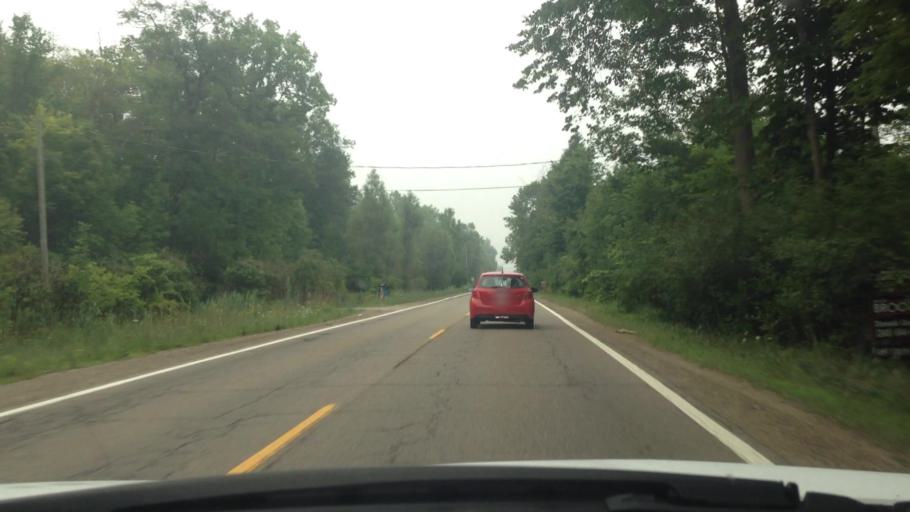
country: US
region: Michigan
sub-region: Oakland County
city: Clarkston
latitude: 42.7298
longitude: -83.3498
